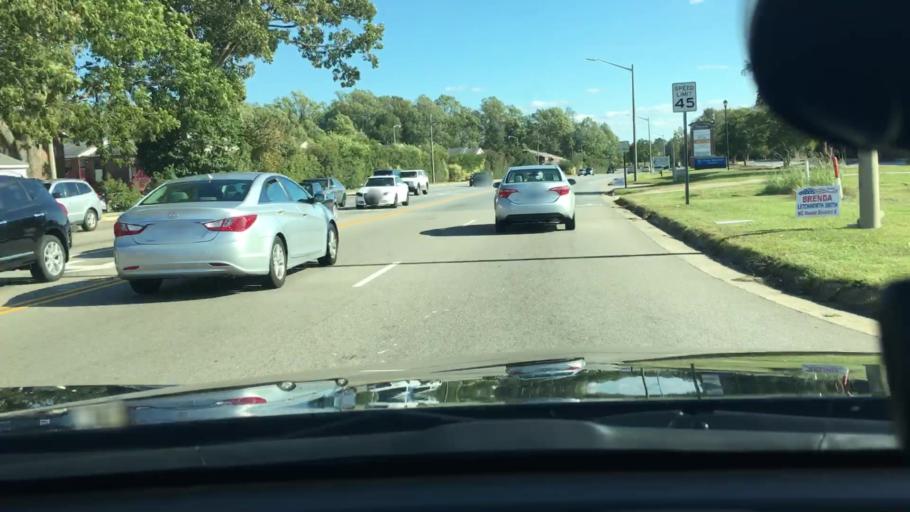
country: US
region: North Carolina
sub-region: Pitt County
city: Summerfield
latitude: 35.5950
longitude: -77.4026
